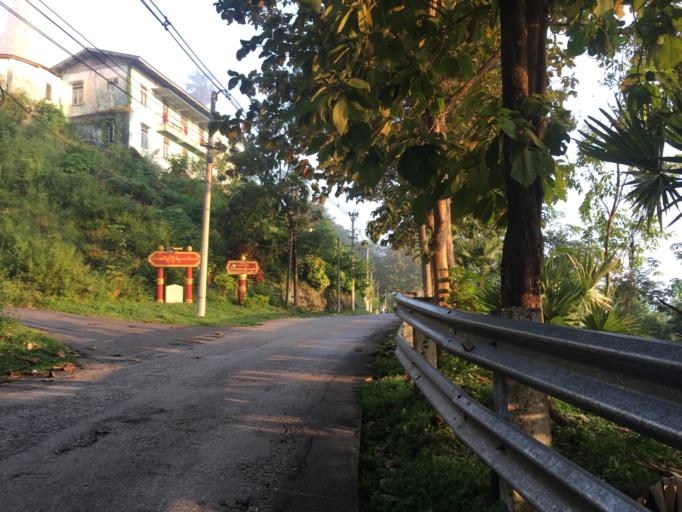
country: MM
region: Mon
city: Mawlamyine
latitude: 16.4725
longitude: 97.6303
